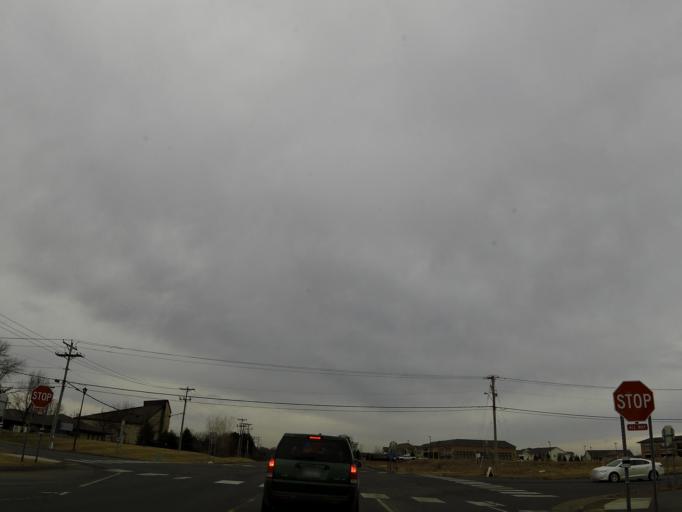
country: US
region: Minnesota
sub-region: Washington County
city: Cottage Grove
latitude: 44.8481
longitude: -92.9487
